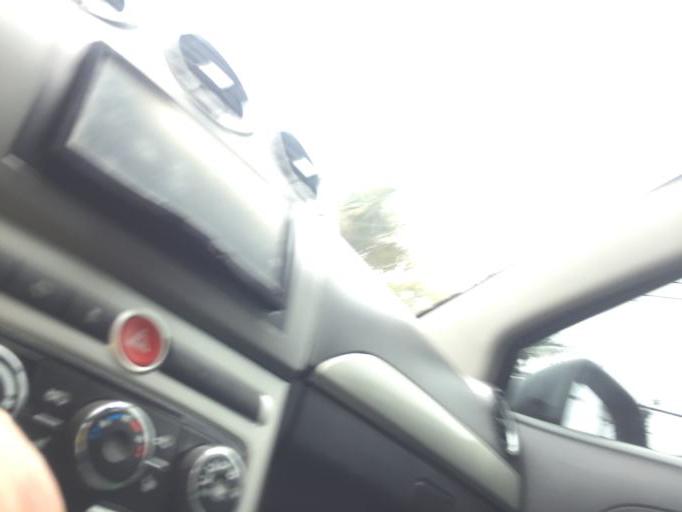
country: CO
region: Cundinamarca
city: El Rosal
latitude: 4.8532
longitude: -74.2606
